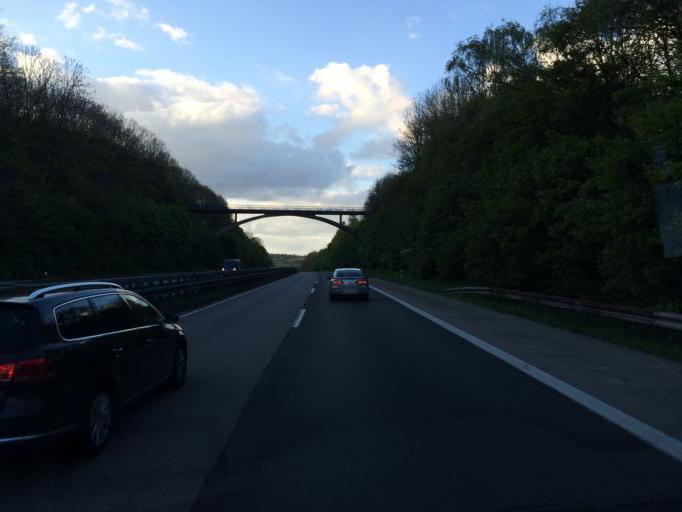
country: DE
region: North Rhine-Westphalia
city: Sprockhovel
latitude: 51.3985
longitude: 7.2643
